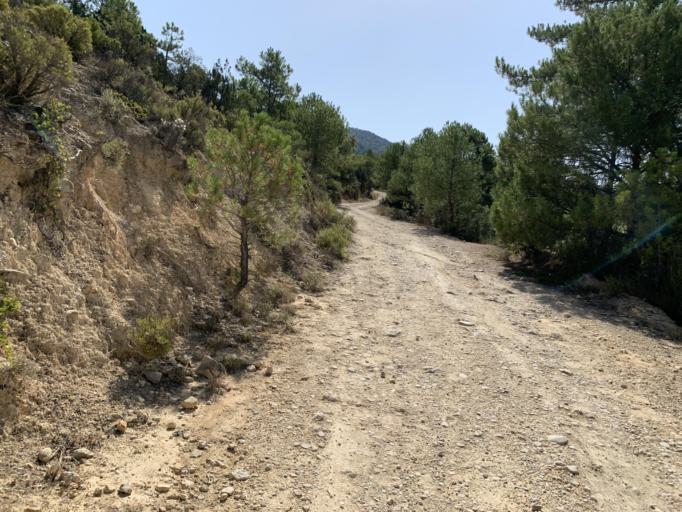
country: ES
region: Castille-La Mancha
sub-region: Provincia de Guadalajara
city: Ocentejo
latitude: 40.7633
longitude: -2.3911
